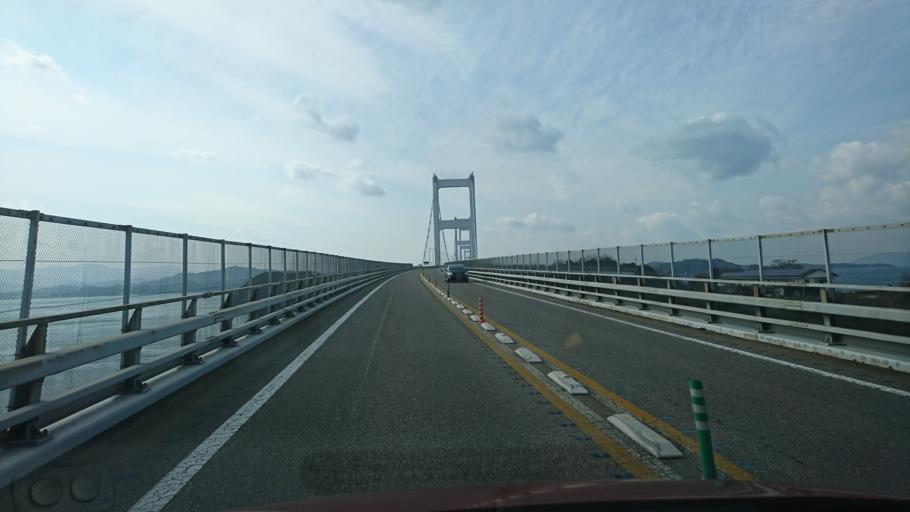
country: JP
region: Hiroshima
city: Innoshima
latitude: 34.1286
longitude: 133.0194
